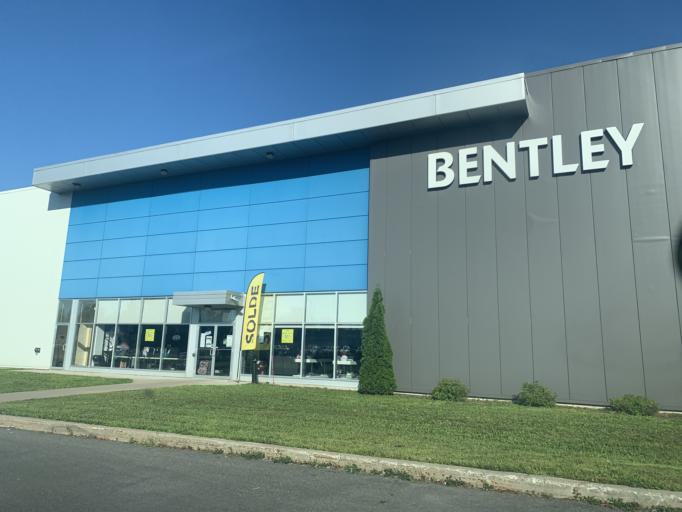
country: CA
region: Ontario
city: Hawkesbury
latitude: 45.5949
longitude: -74.5988
